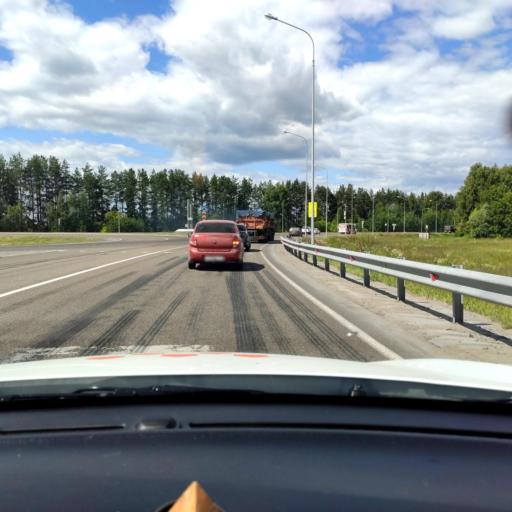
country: RU
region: Mariy-El
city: Volzhsk
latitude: 55.9126
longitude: 48.3675
